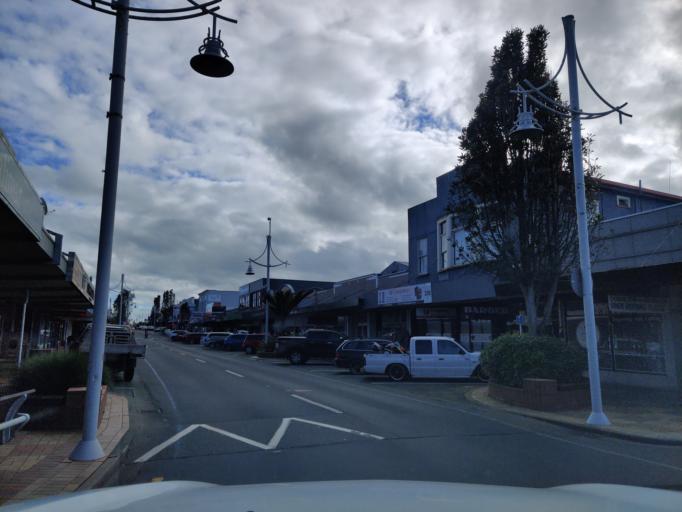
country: NZ
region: Auckland
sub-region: Auckland
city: Pukekohe East
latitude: -37.2009
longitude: 174.9074
